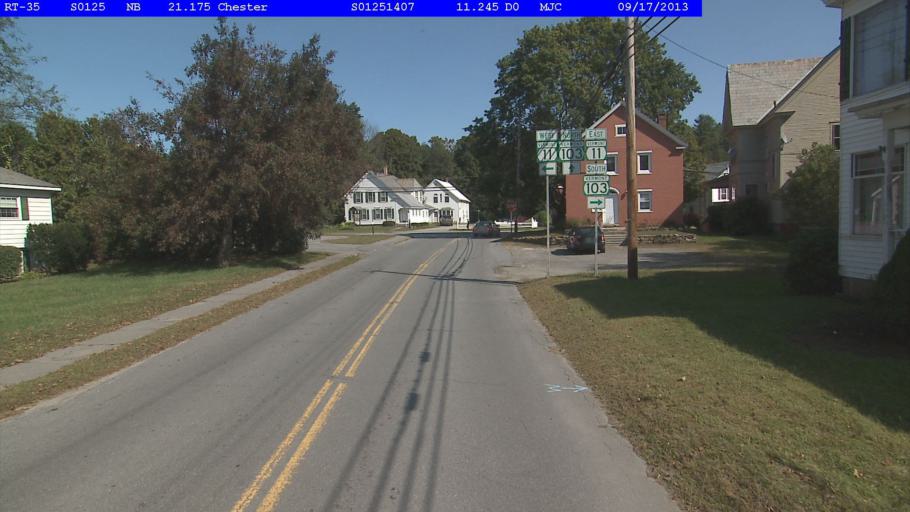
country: US
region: Vermont
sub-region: Windsor County
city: Chester
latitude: 43.2625
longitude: -72.5952
